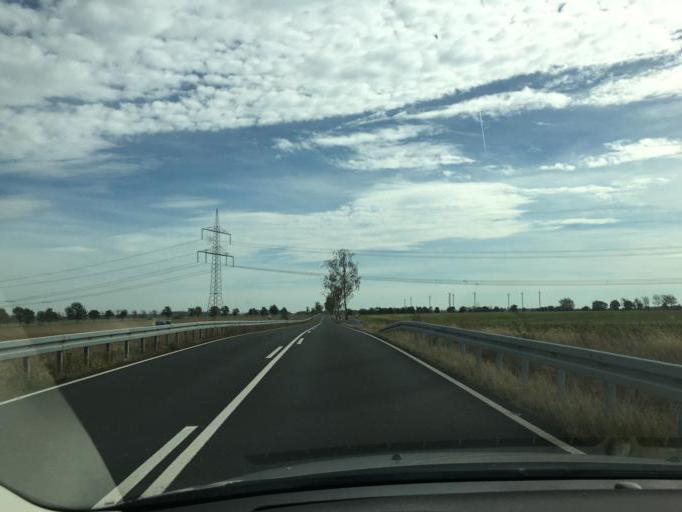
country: DE
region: Saxony
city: Lommatzsch
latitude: 51.2416
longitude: 13.3115
